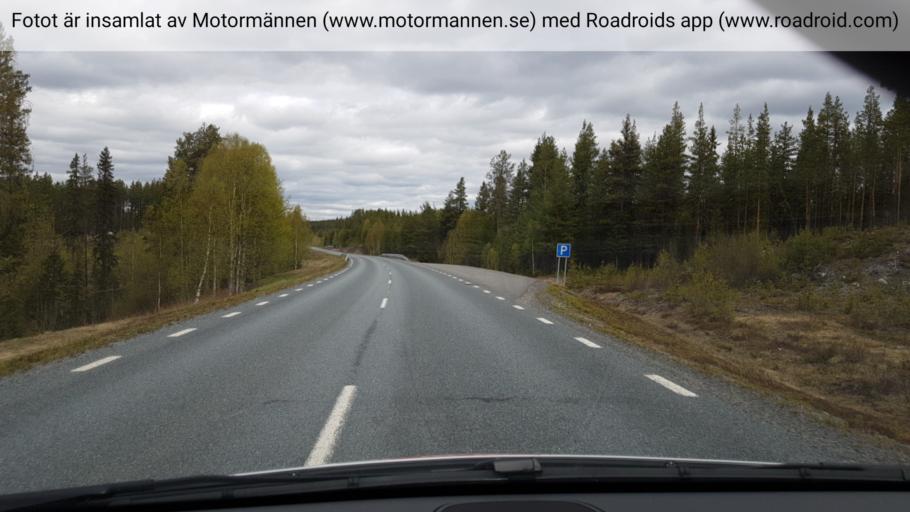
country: SE
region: Vaesterbotten
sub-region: Mala Kommun
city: Mala
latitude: 65.0597
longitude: 18.3798
